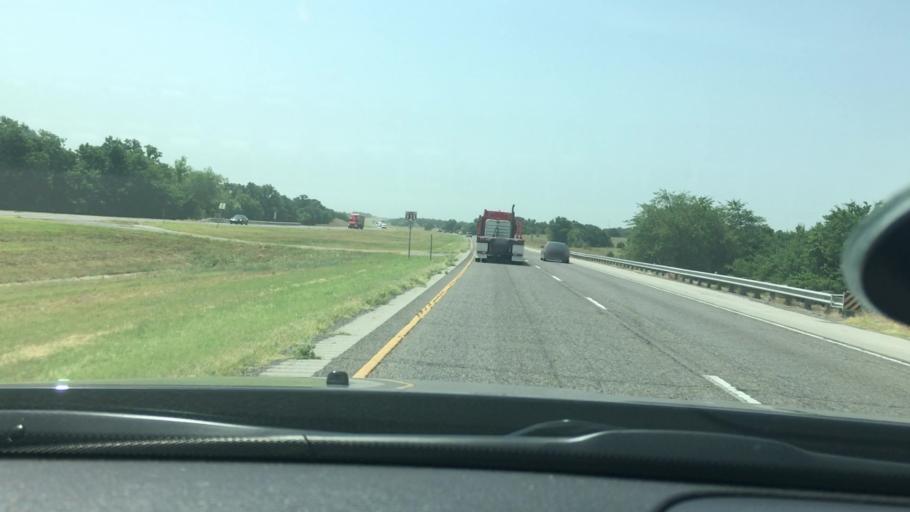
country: US
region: Oklahoma
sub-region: Garvin County
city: Wynnewood
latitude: 34.6029
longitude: -97.2114
